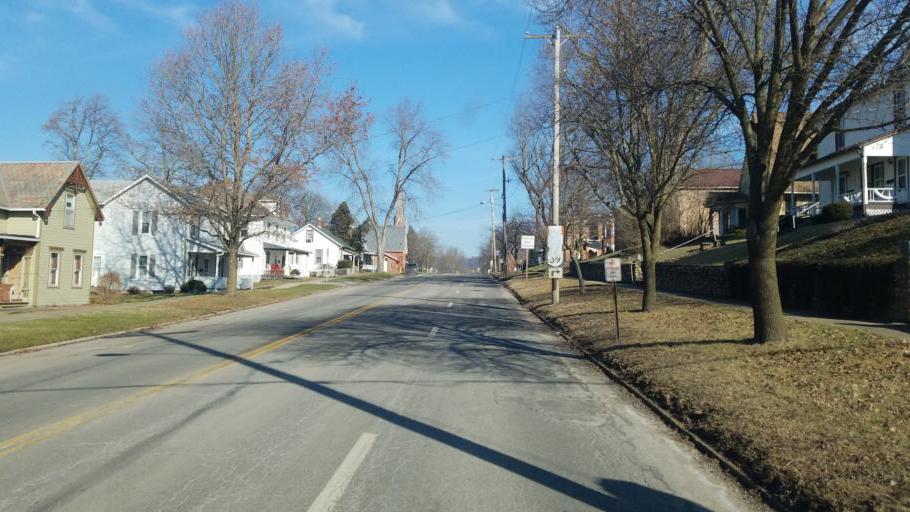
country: US
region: Ohio
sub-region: Ashland County
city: Loudonville
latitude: 40.6332
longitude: -82.2336
